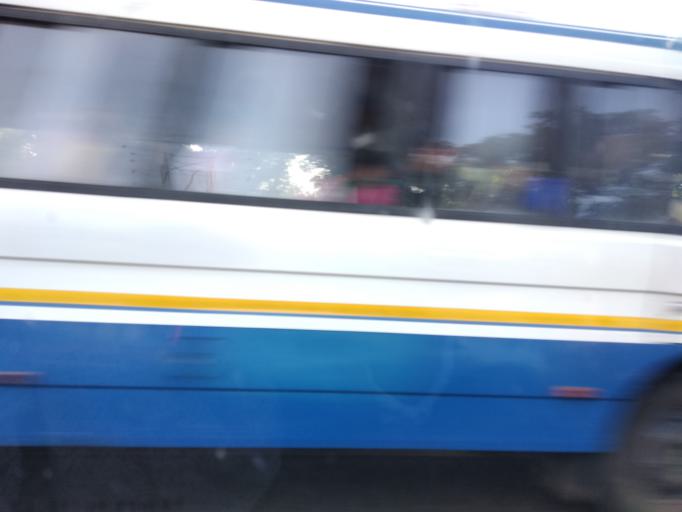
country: IN
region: Andhra Pradesh
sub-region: Vishakhapatnam
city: Visakhapatnam
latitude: 17.6849
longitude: 83.1659
